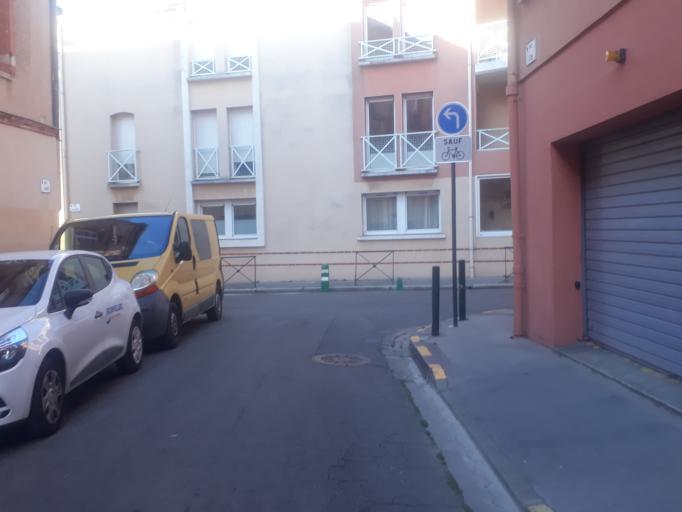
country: FR
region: Midi-Pyrenees
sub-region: Departement de la Haute-Garonne
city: Toulouse
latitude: 43.6121
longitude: 1.4466
